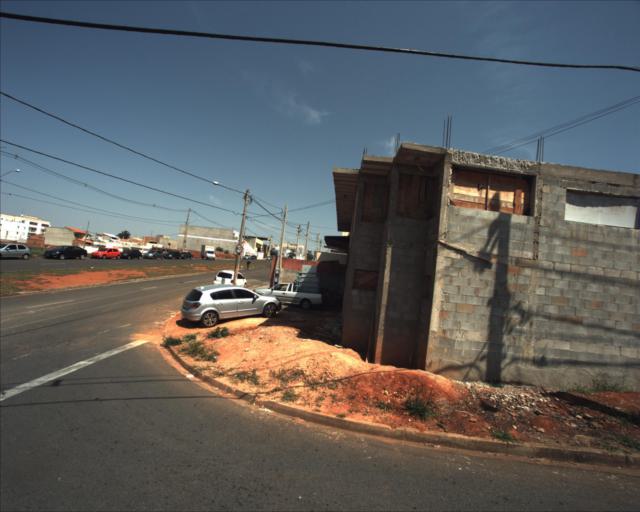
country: BR
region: Sao Paulo
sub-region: Sorocaba
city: Sorocaba
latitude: -23.4642
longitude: -47.4914
